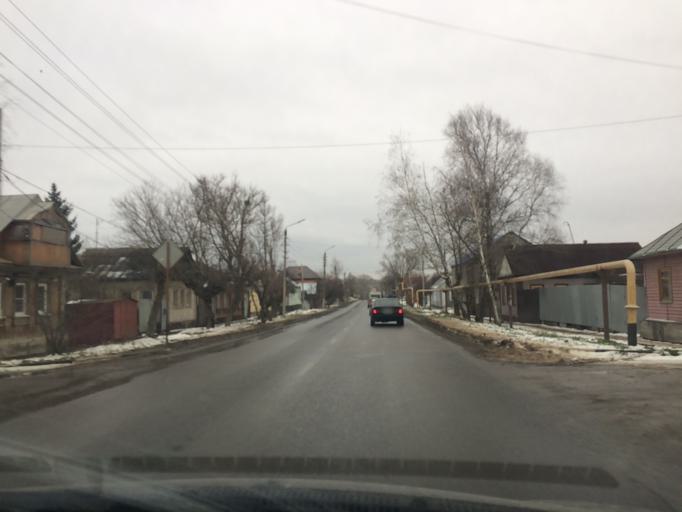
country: RU
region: Tula
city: Gorelki
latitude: 54.2389
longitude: 37.6410
